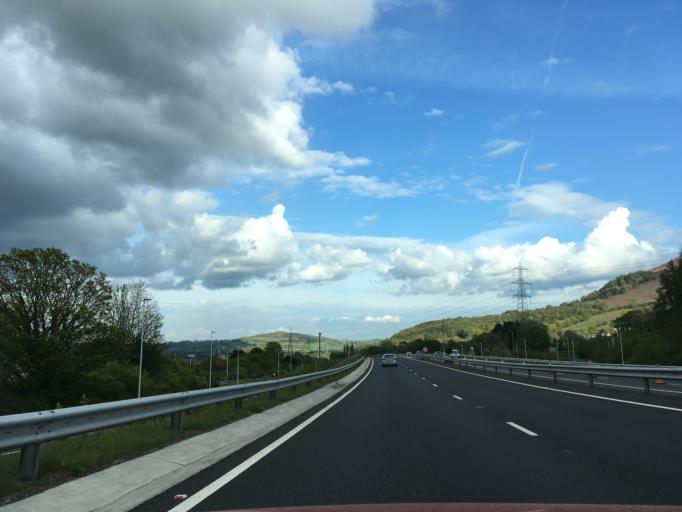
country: GB
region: Wales
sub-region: Monmouthshire
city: Gilwern
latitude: 51.8234
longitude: -3.0790
